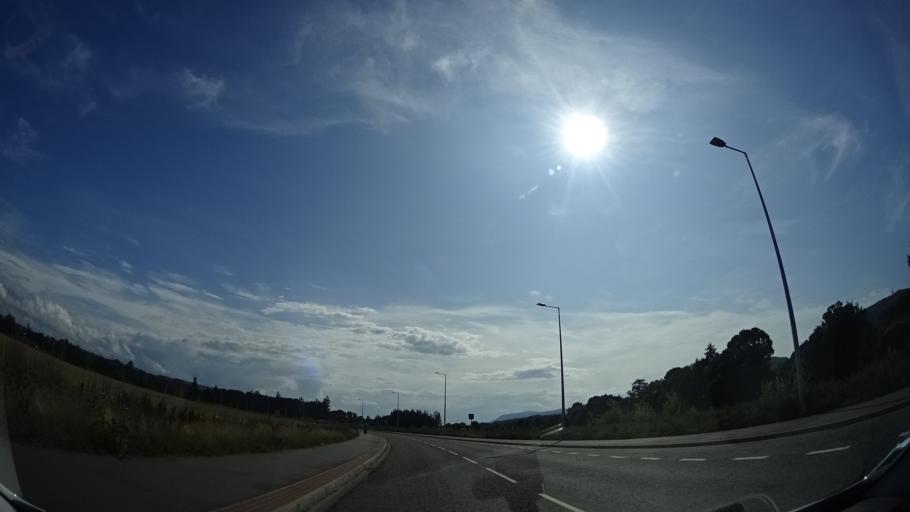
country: GB
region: Scotland
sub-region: Highland
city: Inverness
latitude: 57.4557
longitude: -4.2555
